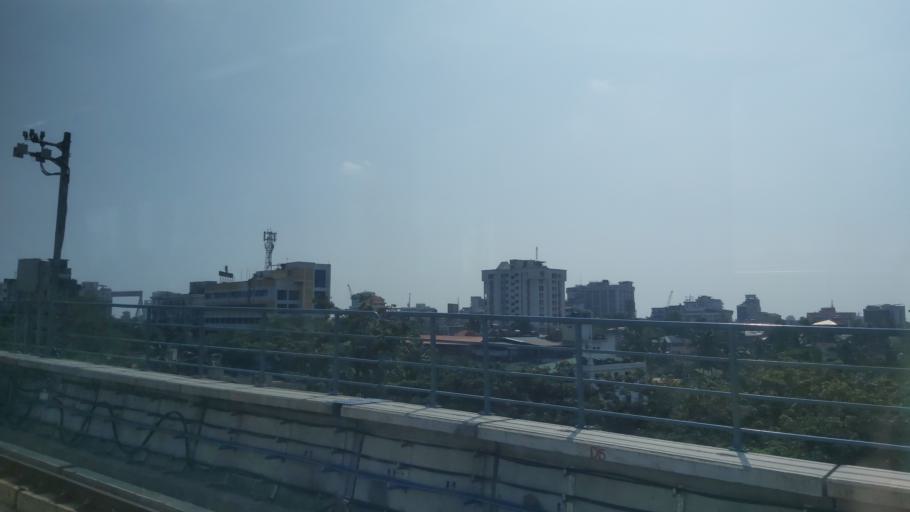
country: IN
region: Kerala
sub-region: Ernakulam
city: Cochin
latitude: 9.9675
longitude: 76.2914
